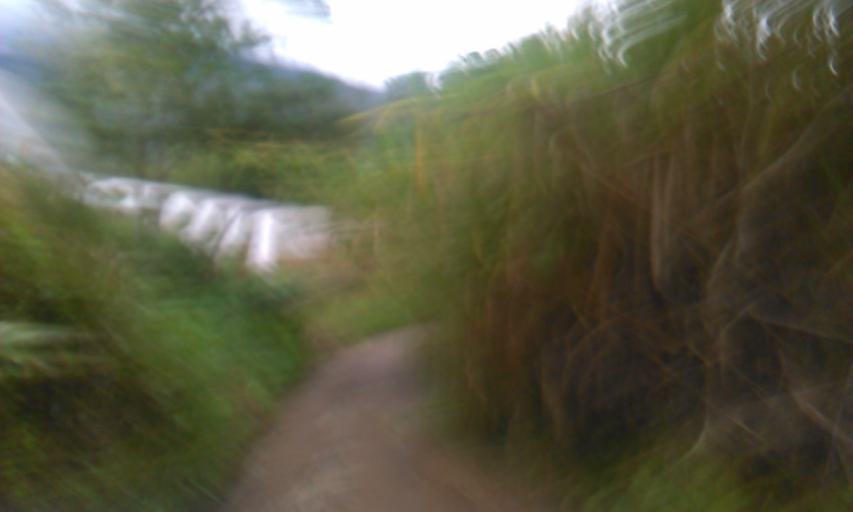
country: CO
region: Quindio
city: Cordoba
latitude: 4.4048
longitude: -75.6888
